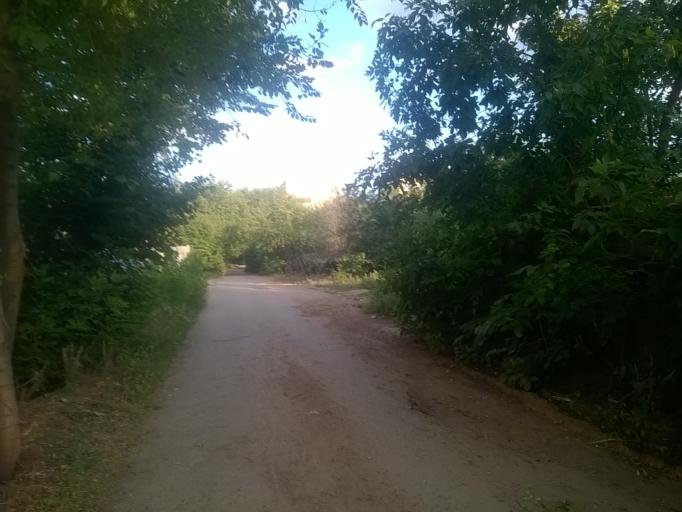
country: RU
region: Rostov
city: Donetsk
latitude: 48.3326
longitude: 39.9600
